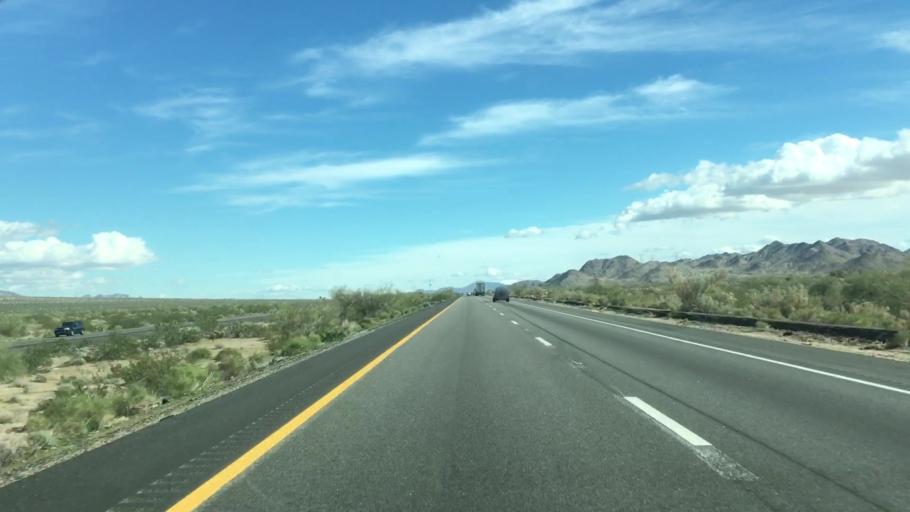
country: US
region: California
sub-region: Riverside County
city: Mecca
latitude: 33.6599
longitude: -115.7616
